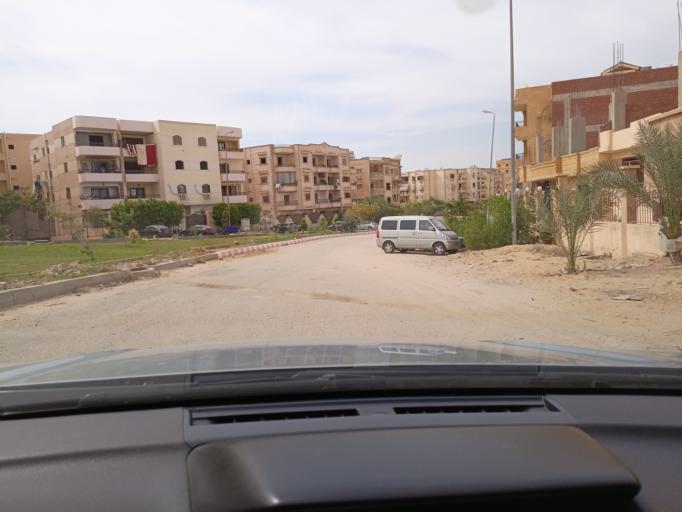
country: EG
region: Muhafazat al Qalyubiyah
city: Al Khankah
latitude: 30.2433
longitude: 31.4899
